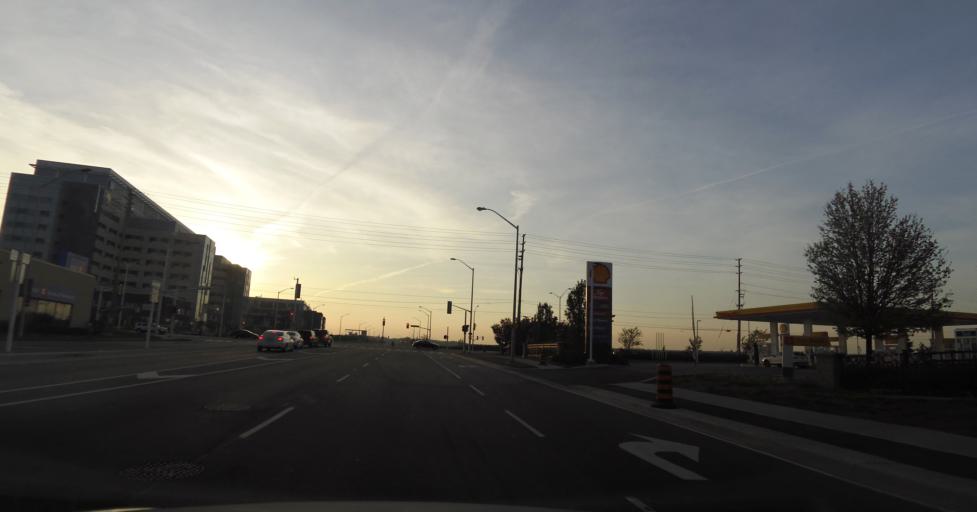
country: CA
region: Ontario
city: Oakville
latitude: 43.4497
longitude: -79.7600
